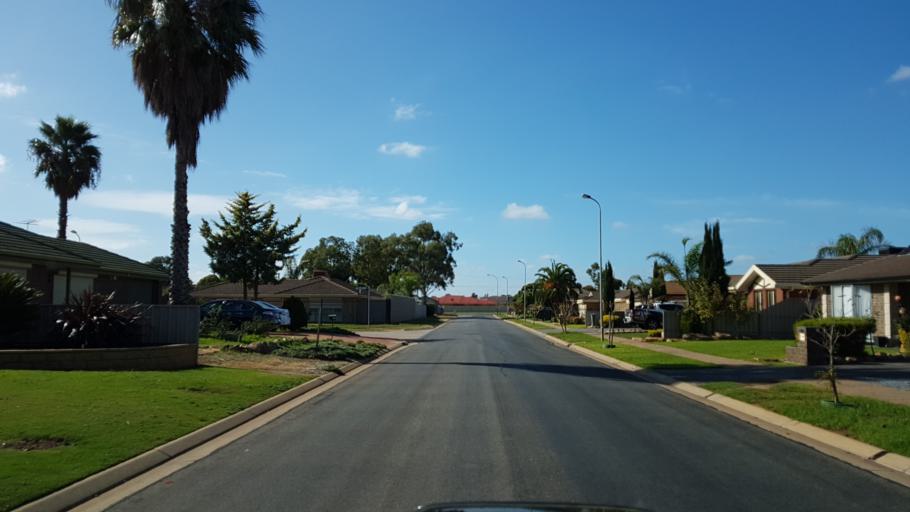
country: AU
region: South Australia
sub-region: Salisbury
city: Salisbury
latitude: -34.7351
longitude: 138.6150
